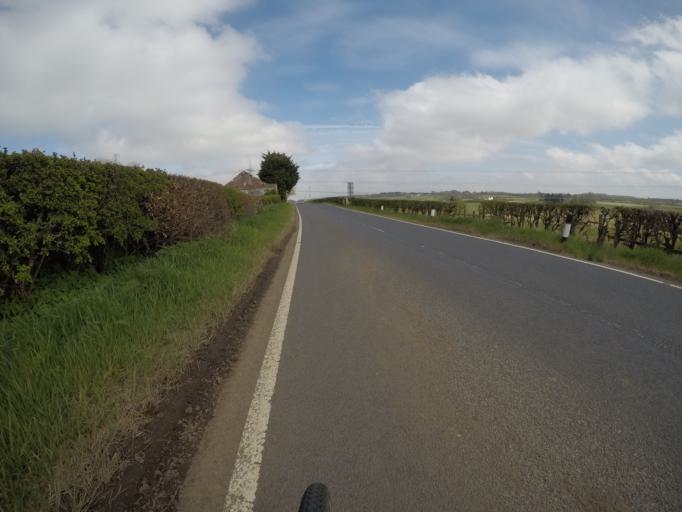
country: GB
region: Scotland
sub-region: East Ayrshire
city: Stewarton
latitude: 55.7033
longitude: -4.4732
